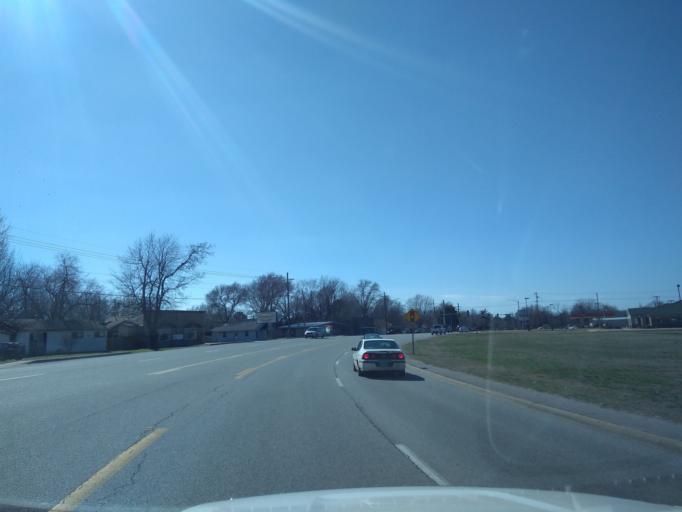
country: US
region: Arkansas
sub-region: Washington County
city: Farmington
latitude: 36.0430
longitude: -94.2338
